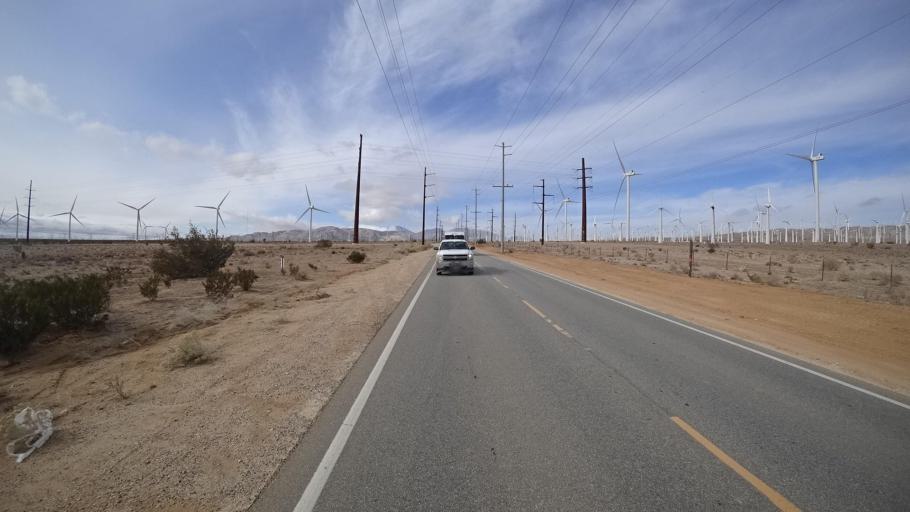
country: US
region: California
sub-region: Kern County
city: Mojave
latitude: 35.0387
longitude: -118.2649
